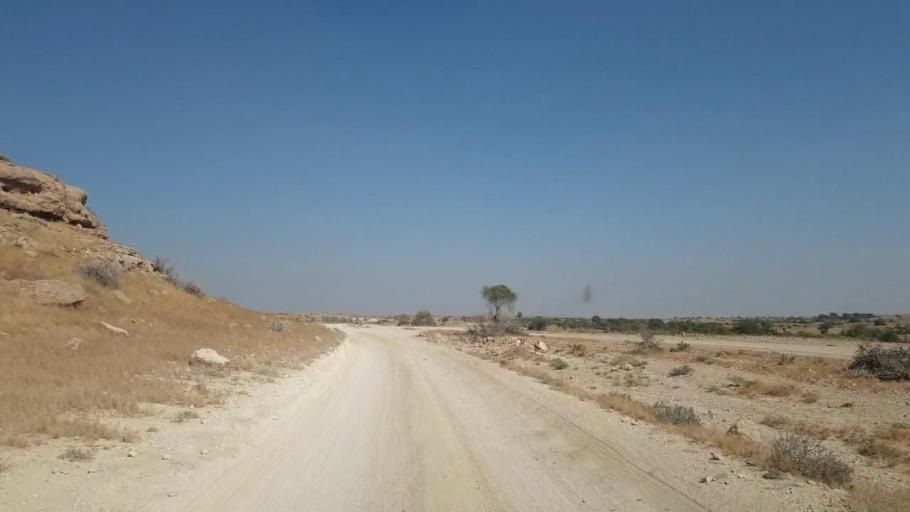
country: PK
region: Sindh
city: Thatta
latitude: 25.2215
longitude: 67.7998
